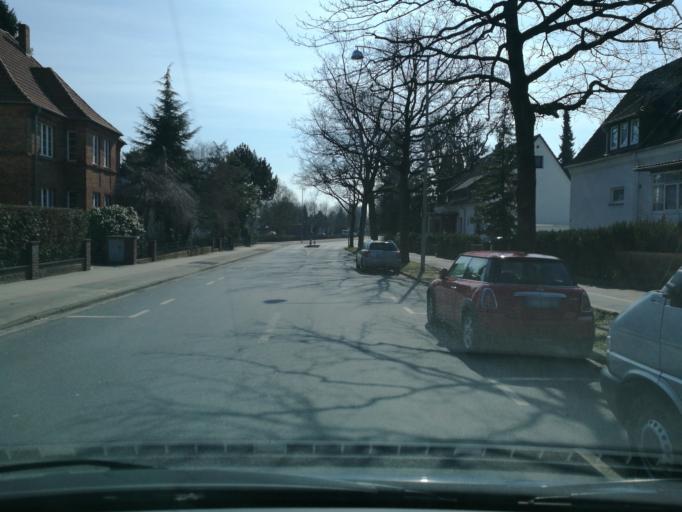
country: DE
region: Lower Saxony
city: Ronnenberg
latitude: 52.3710
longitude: 9.6692
